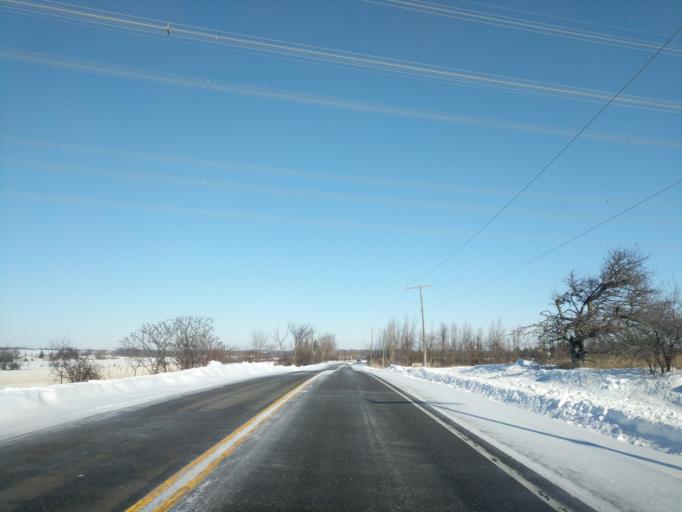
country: CA
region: Ontario
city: Pickering
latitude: 43.8521
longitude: -79.1302
